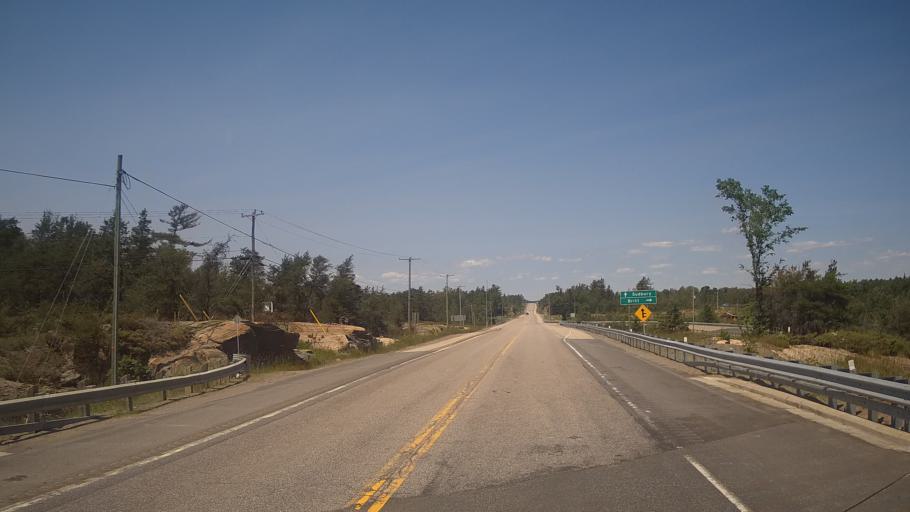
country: CA
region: Ontario
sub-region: Parry Sound District
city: Parry Sound
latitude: 45.8009
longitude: -80.5365
